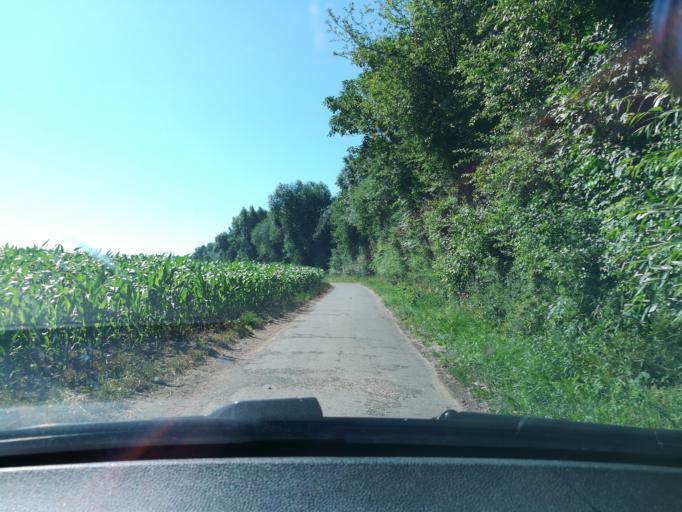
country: DE
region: North Rhine-Westphalia
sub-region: Regierungsbezirk Detmold
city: Minden
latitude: 52.3116
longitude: 8.9230
